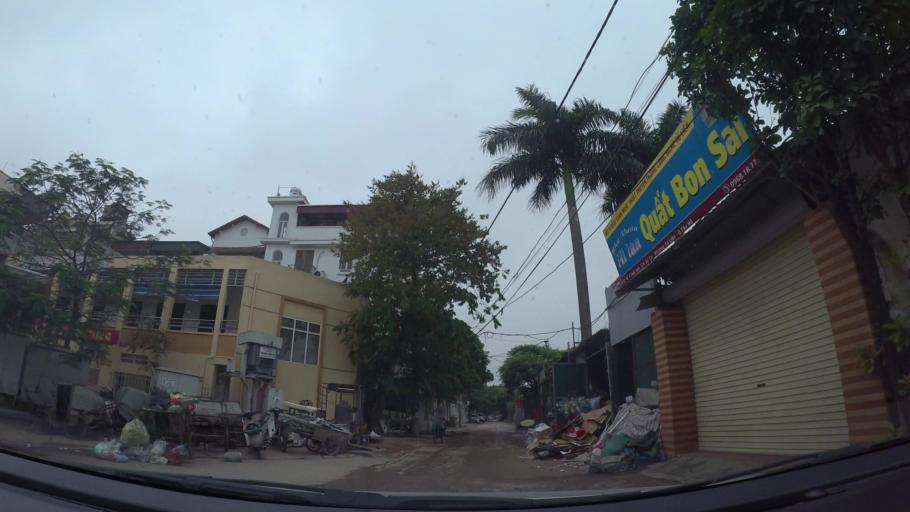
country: VN
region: Ha Noi
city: Tay Ho
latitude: 21.0657
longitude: 105.8369
